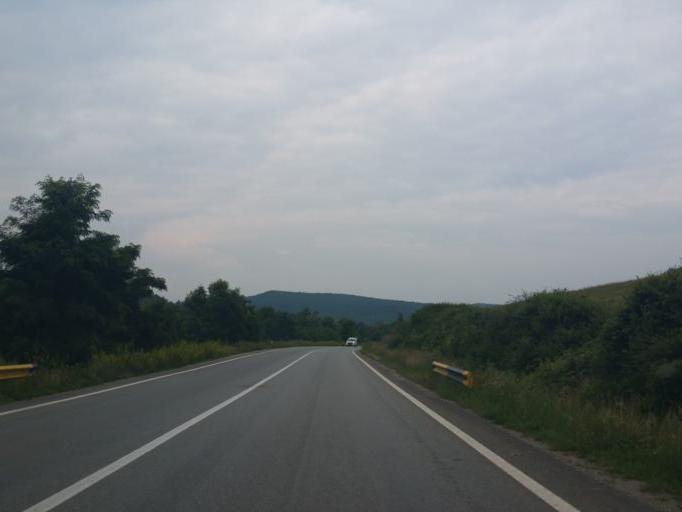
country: RO
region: Salaj
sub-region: Comuna Zimbor
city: Zimbor
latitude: 46.9769
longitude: 23.2537
